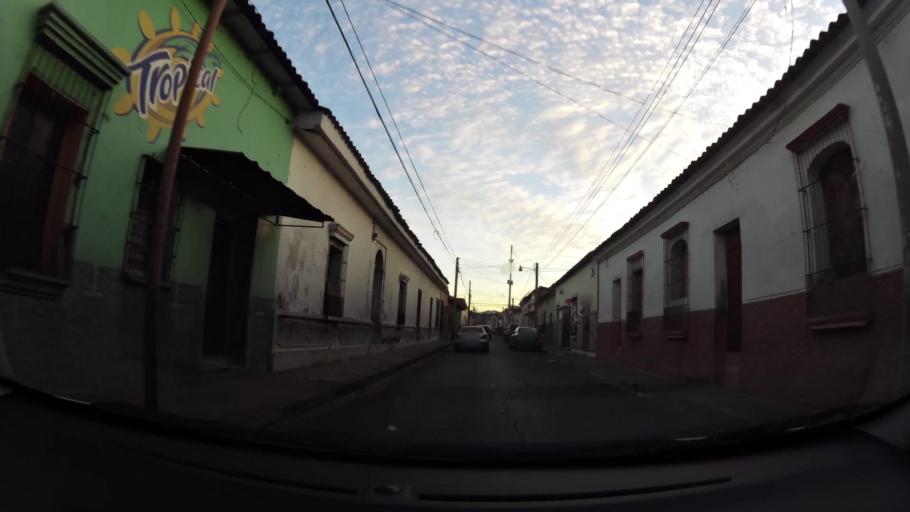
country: SV
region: Santa Ana
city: Santa Ana
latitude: 13.9959
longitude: -89.5532
